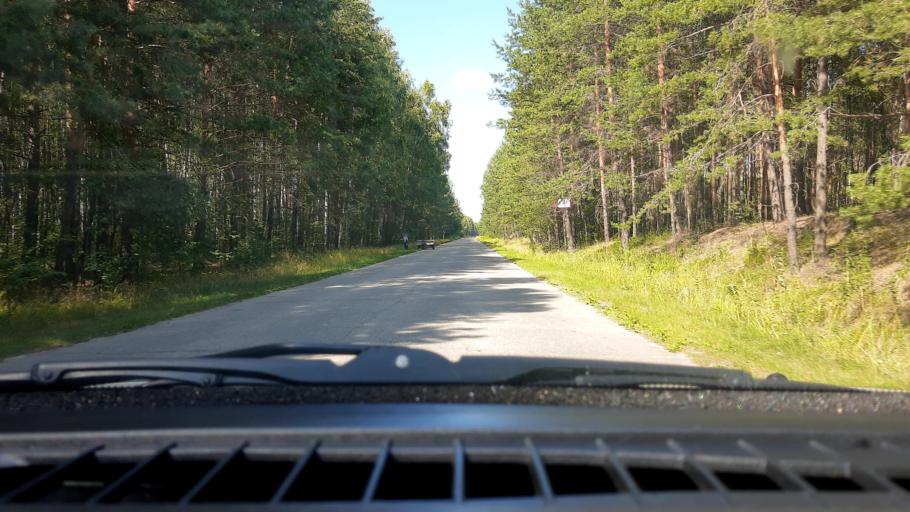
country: RU
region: Nizjnij Novgorod
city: Babino
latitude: 56.3263
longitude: 43.6343
